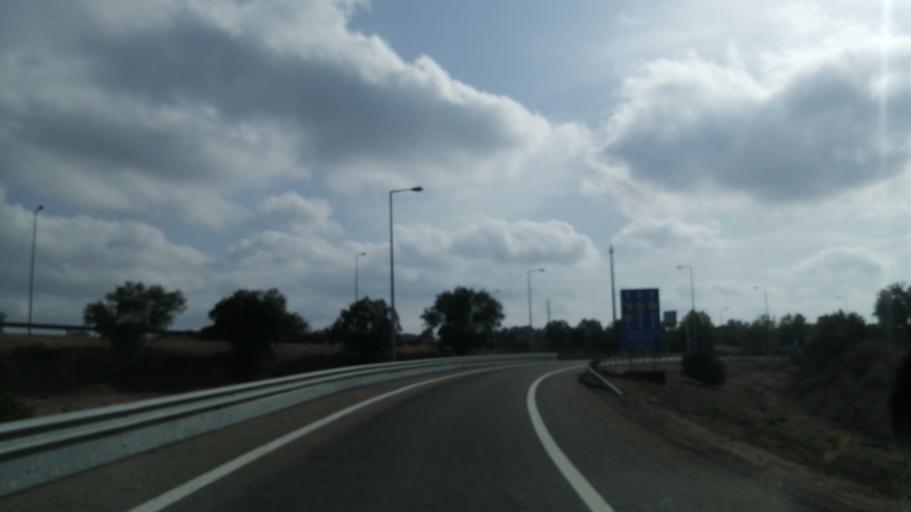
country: PT
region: Evora
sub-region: Montemor-O-Novo
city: Montemor-o-Novo
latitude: 38.6657
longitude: -8.2332
